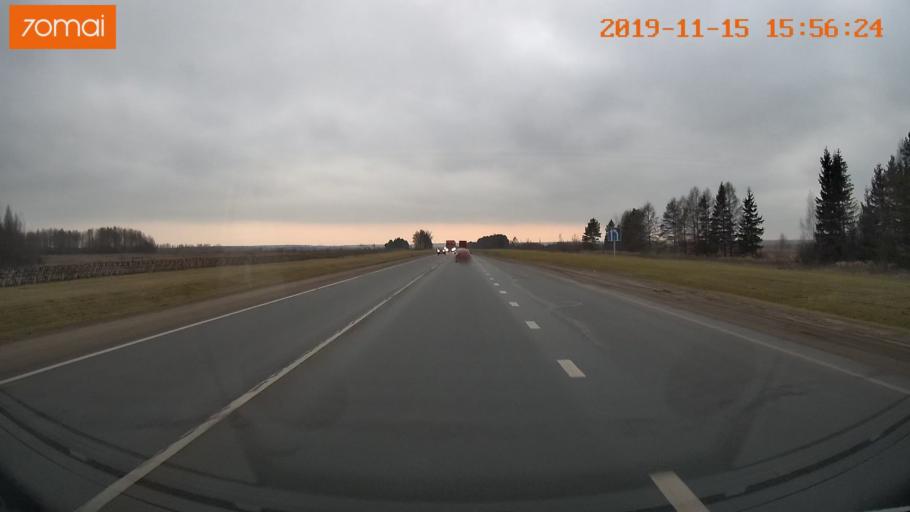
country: RU
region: Jaroslavl
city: Yaroslavl
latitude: 57.8425
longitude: 39.9740
